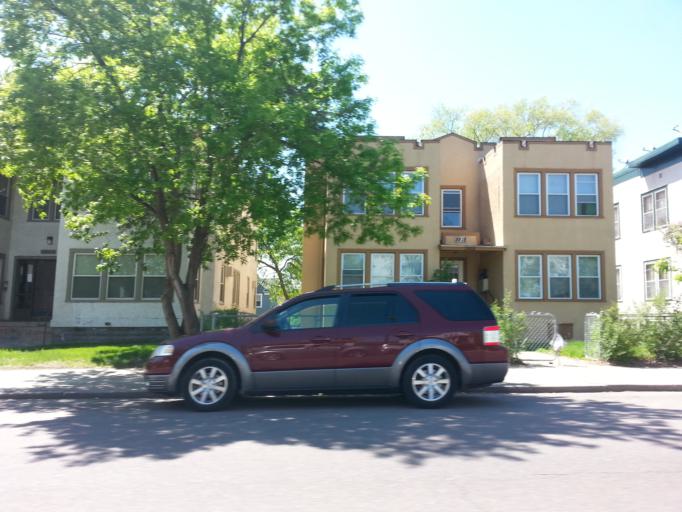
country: US
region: Minnesota
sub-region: Hennepin County
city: Minneapolis
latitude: 44.9334
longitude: -93.2625
